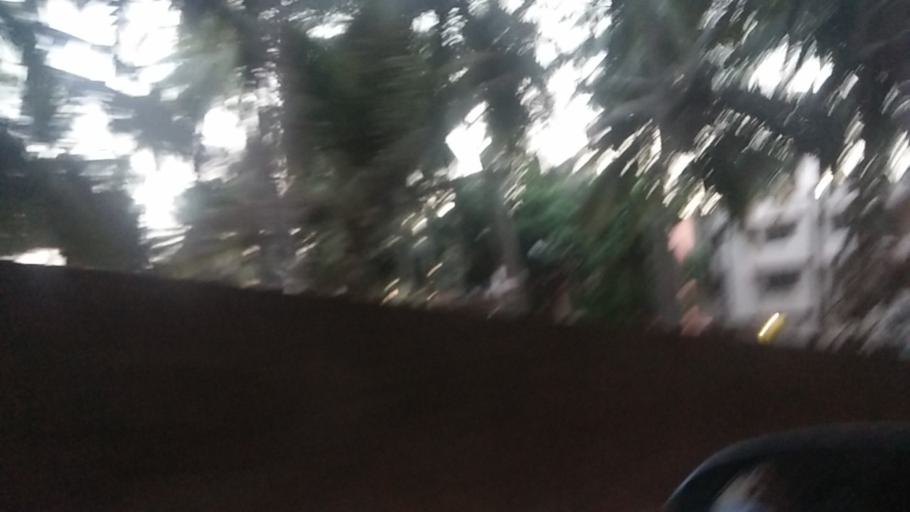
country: IN
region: Goa
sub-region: North Goa
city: Bambolim
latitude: 15.4704
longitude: 73.8449
